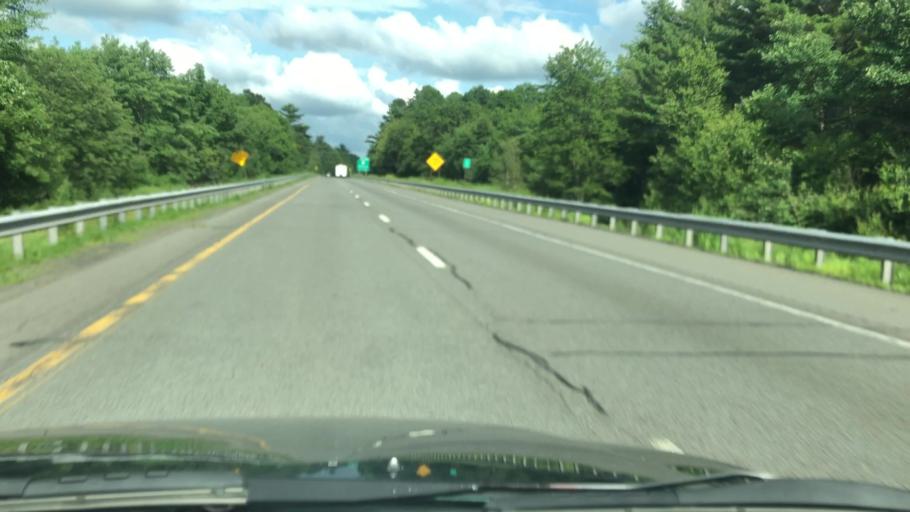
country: US
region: Pennsylvania
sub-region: Pike County
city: Gold Key Lake
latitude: 41.3403
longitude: -74.8812
